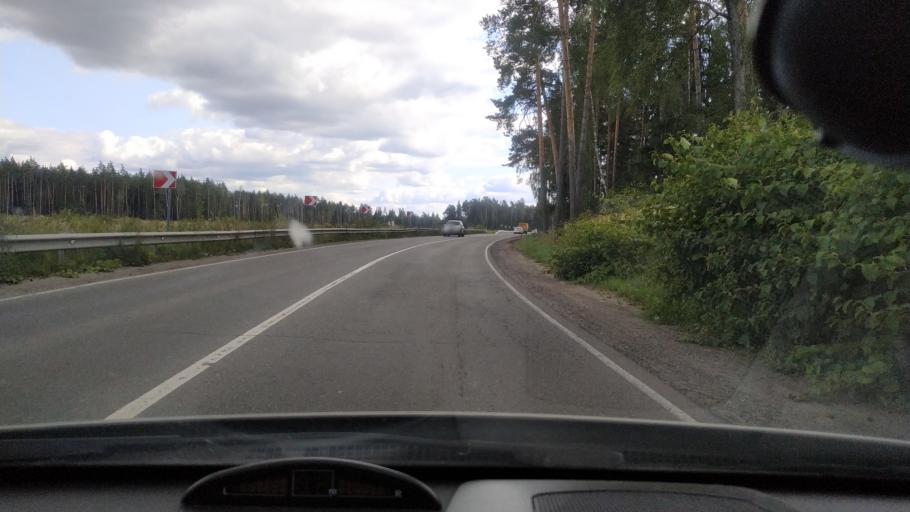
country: RU
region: Moskovskaya
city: Chornaya
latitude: 55.7737
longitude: 38.0521
